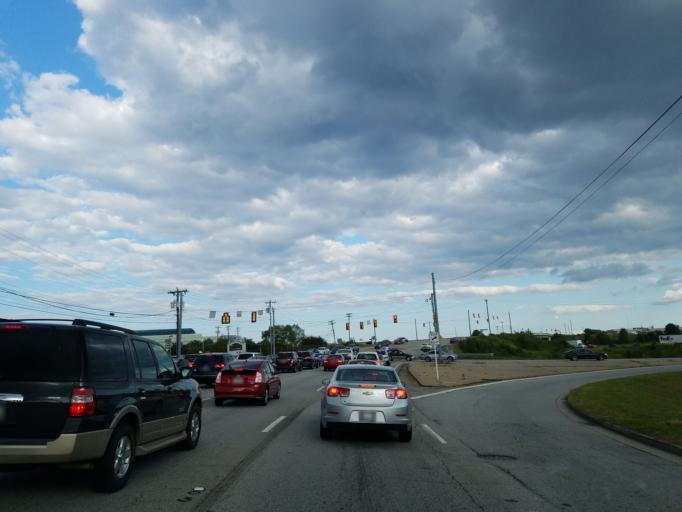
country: US
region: South Carolina
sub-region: Greenville County
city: Five Forks
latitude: 34.8597
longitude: -82.2630
